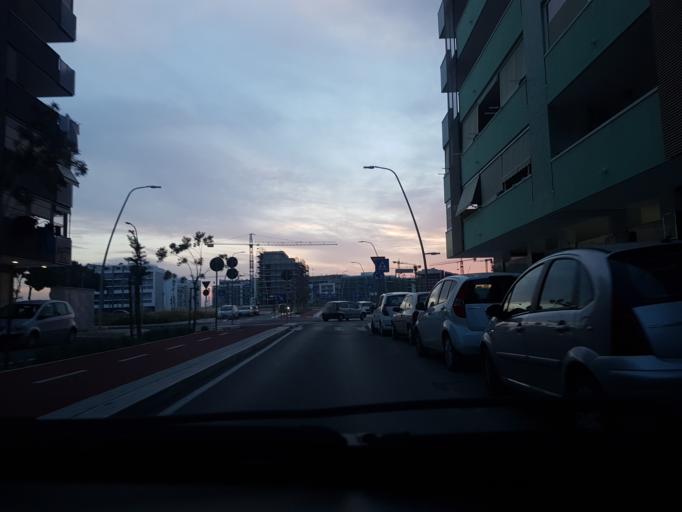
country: IT
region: Apulia
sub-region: Provincia di Barletta - Andria - Trani
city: Barletta
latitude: 41.3045
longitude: 16.2719
